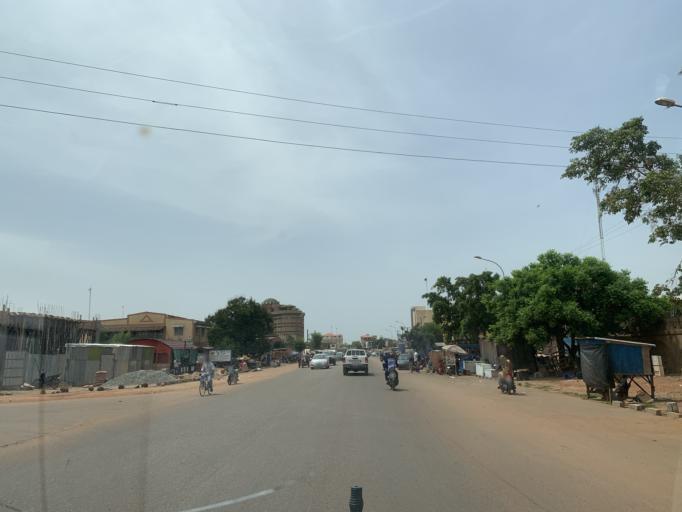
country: BF
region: Centre
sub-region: Kadiogo Province
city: Ouagadougou
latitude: 12.3370
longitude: -1.5009
